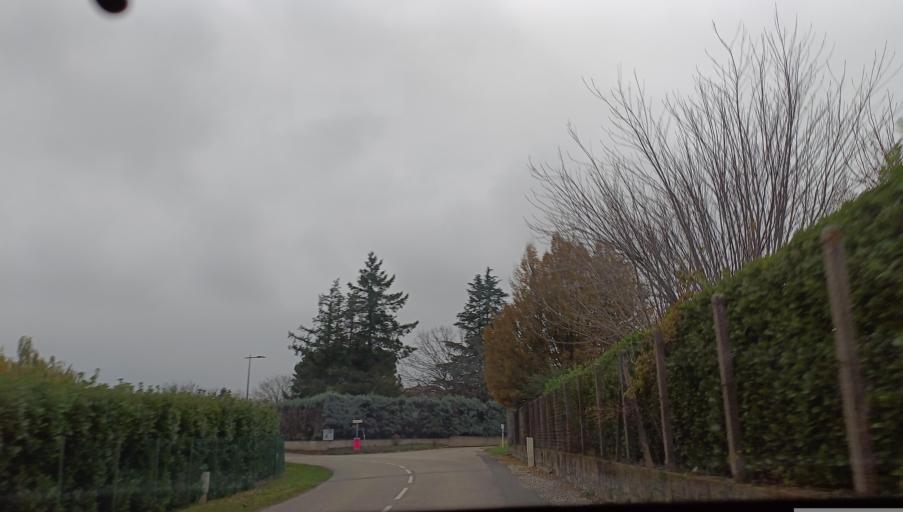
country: FR
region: Rhone-Alpes
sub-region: Departement de l'Isere
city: Serpaize
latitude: 45.5564
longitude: 4.9242
